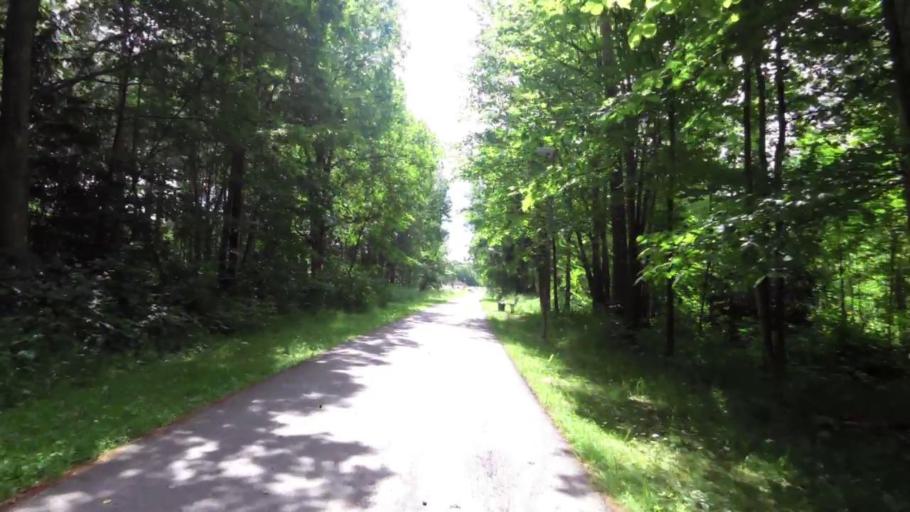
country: SE
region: OEstergoetland
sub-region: Linkopings Kommun
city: Linkoping
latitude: 58.4081
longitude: 15.5804
